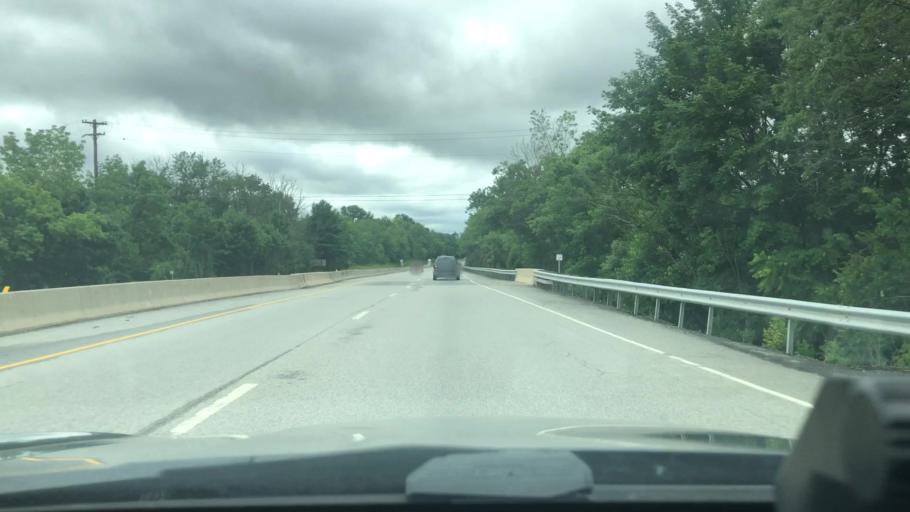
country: US
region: Pennsylvania
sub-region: Montgomery County
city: Halfway House
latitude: 40.2867
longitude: -75.6441
